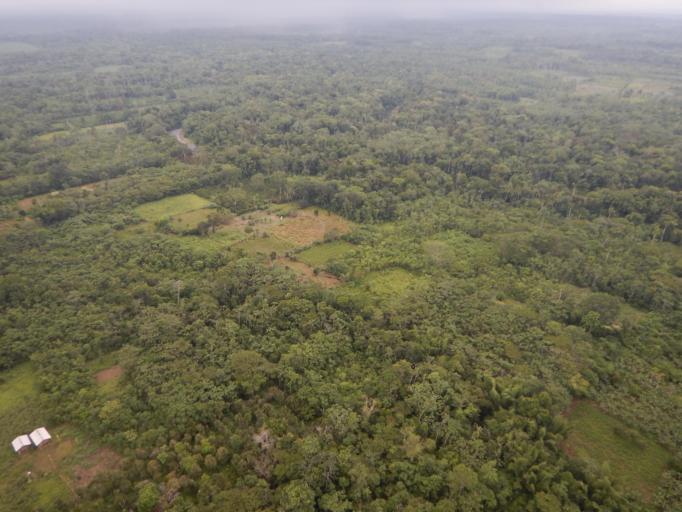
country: BO
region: Cochabamba
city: Chimore
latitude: -17.0997
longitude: -64.8323
